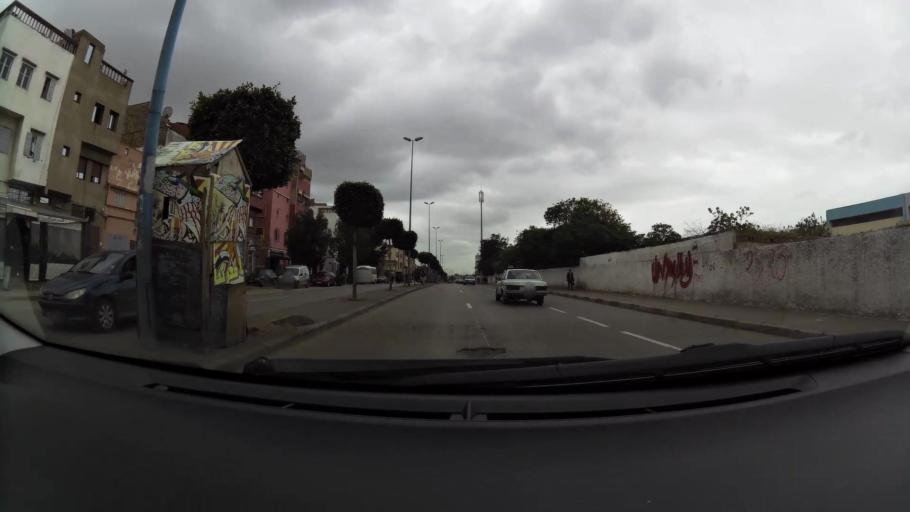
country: MA
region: Grand Casablanca
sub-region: Casablanca
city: Casablanca
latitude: 33.5589
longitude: -7.5554
